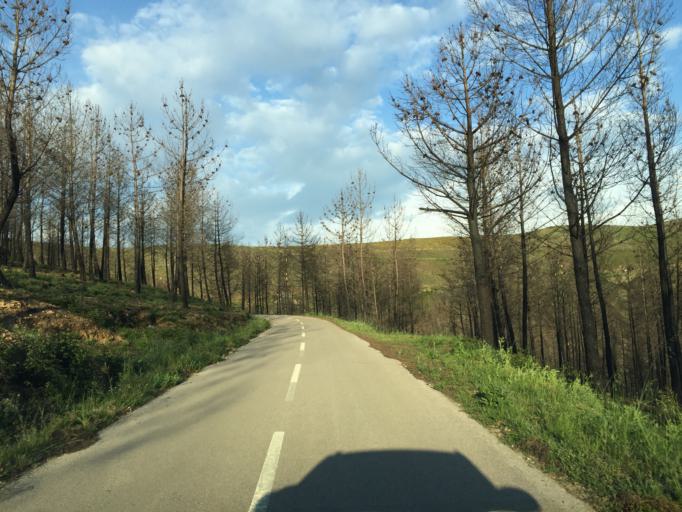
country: PT
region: Coimbra
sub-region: Gois
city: Gois
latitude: 40.1236
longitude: -8.0163
